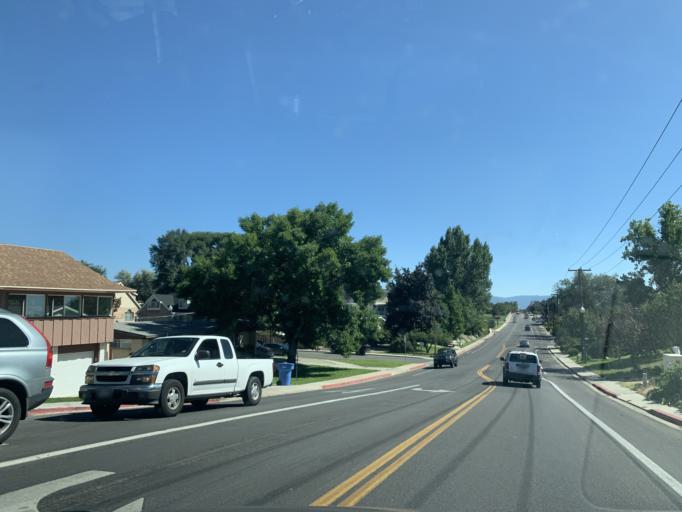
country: US
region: Utah
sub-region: Utah County
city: Orem
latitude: 40.2824
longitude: -111.7049
